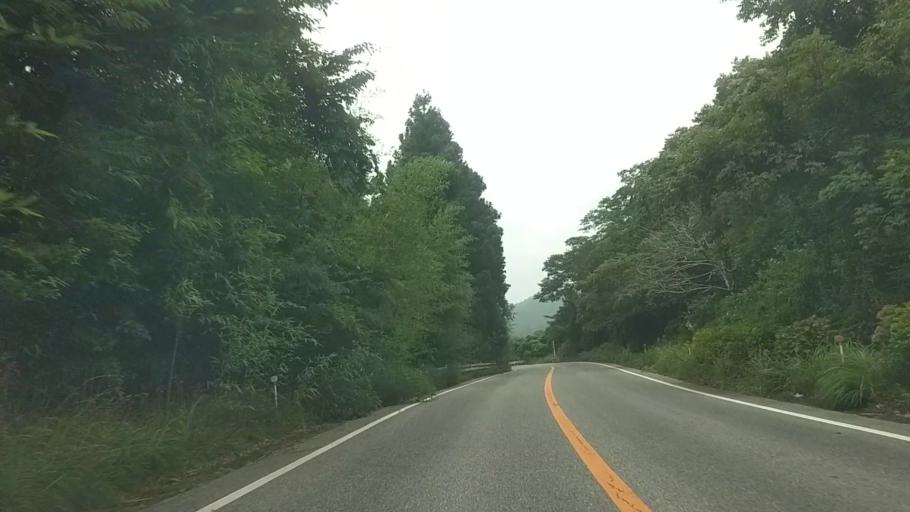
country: JP
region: Chiba
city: Kimitsu
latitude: 35.2418
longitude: 140.0064
